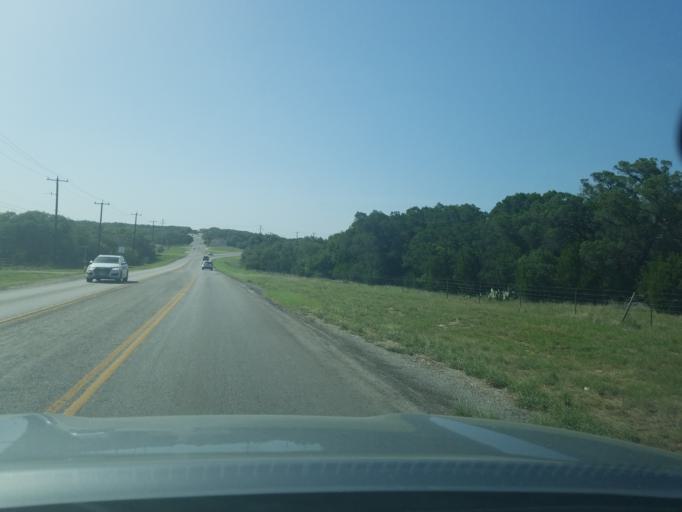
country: US
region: Texas
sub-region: Comal County
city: Garden Ridge
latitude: 29.6880
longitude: -98.3303
